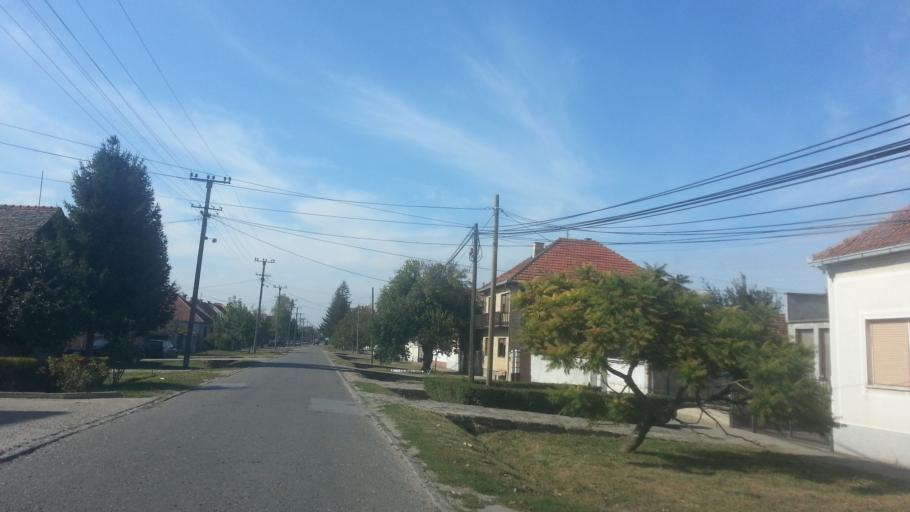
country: RS
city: Belegis
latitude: 45.0219
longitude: 20.3293
